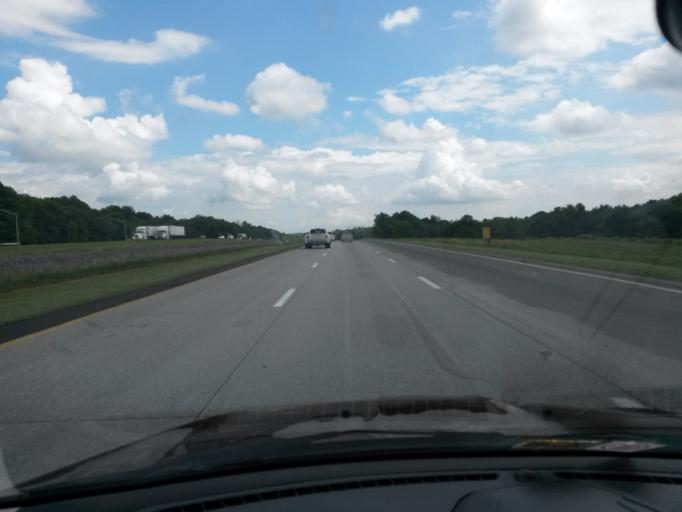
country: US
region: Virginia
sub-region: Carroll County
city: Cana
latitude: 36.5309
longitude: -80.7499
